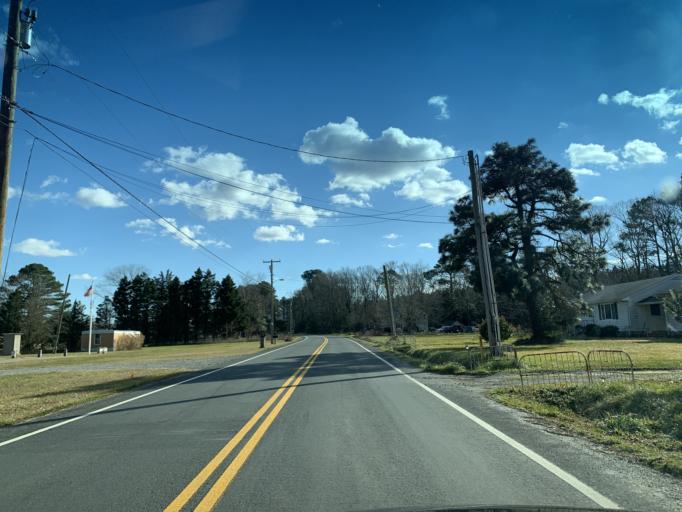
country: US
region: Maryland
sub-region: Worcester County
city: Berlin
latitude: 38.3626
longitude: -75.2007
